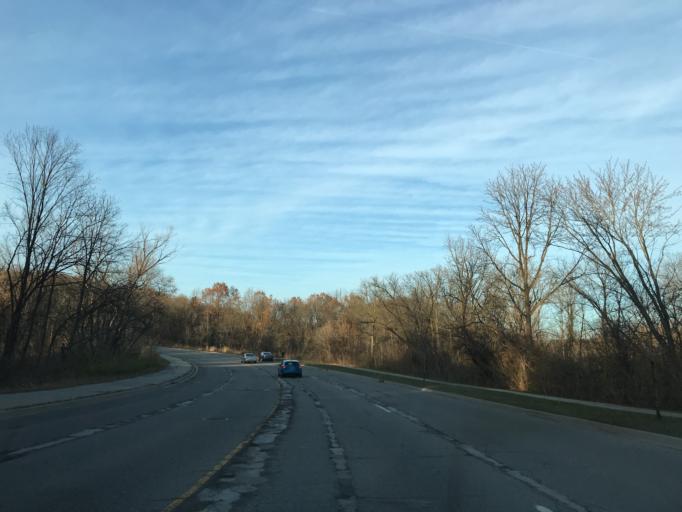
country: US
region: Michigan
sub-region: Washtenaw County
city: Ann Arbor
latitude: 42.2620
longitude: -83.6926
